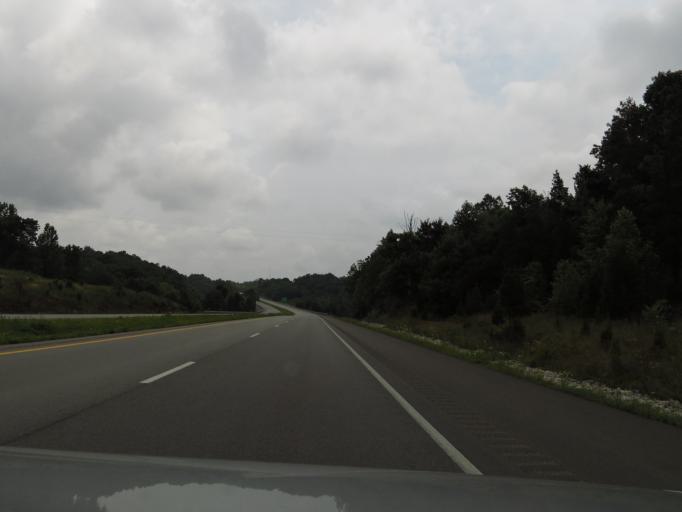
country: US
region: Kentucky
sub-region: Grayson County
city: Leitchfield
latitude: 37.4517
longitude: -86.3268
